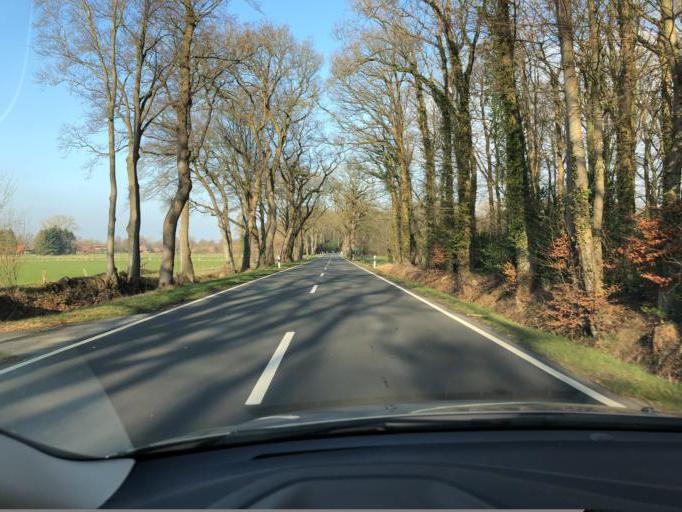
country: DE
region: Lower Saxony
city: Westerstede
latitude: 53.2667
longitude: 7.9095
